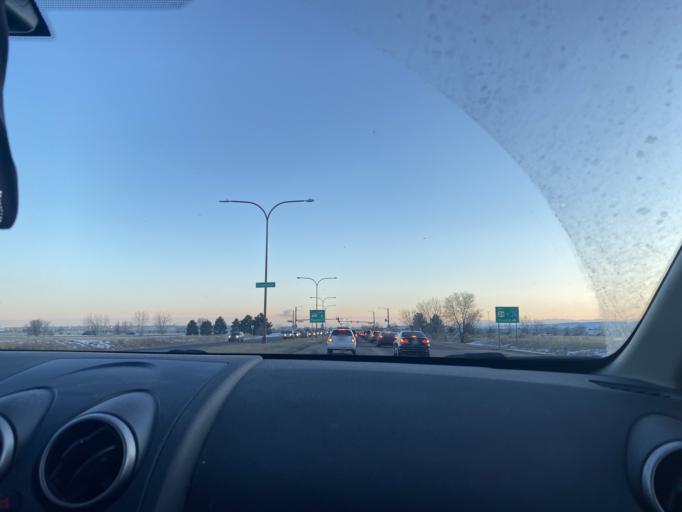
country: US
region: Colorado
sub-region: El Paso County
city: Cimarron Hills
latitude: 38.8086
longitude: -104.7303
